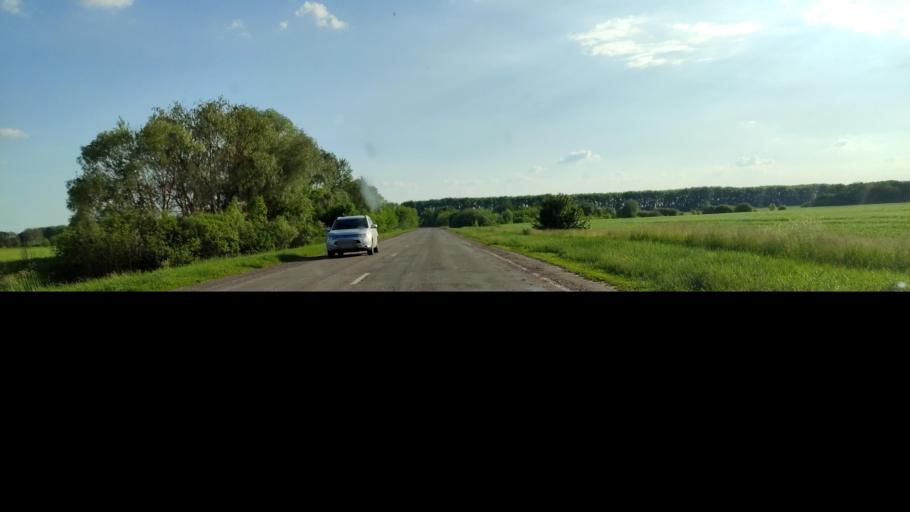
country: RU
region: Voronezj
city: Panino
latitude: 51.6012
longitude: 39.9819
